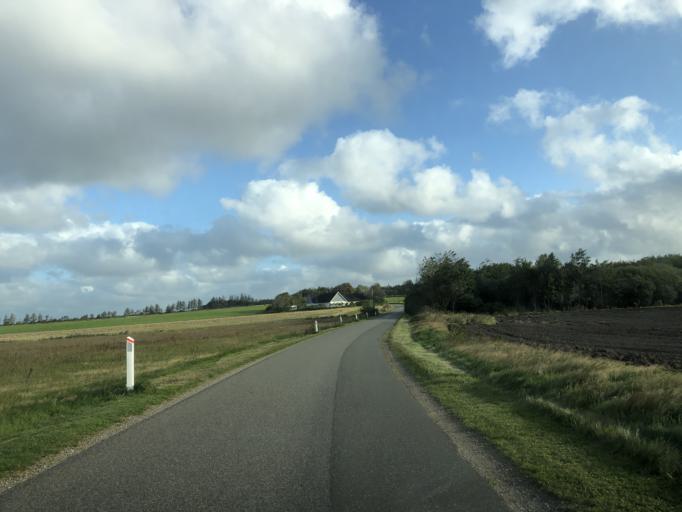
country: DK
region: Central Jutland
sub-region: Holstebro Kommune
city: Ulfborg
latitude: 56.3822
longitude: 8.3462
